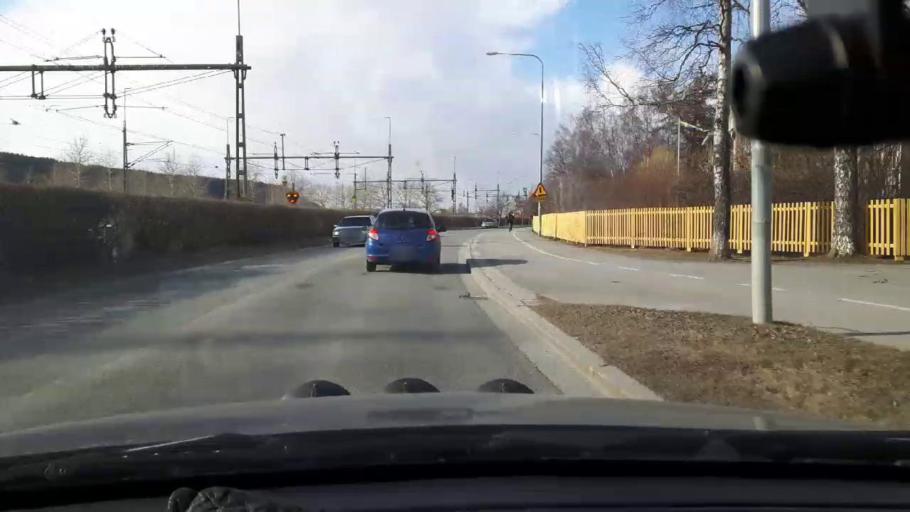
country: SE
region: Jaemtland
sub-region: OEstersunds Kommun
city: Ostersund
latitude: 63.1737
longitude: 14.6328
